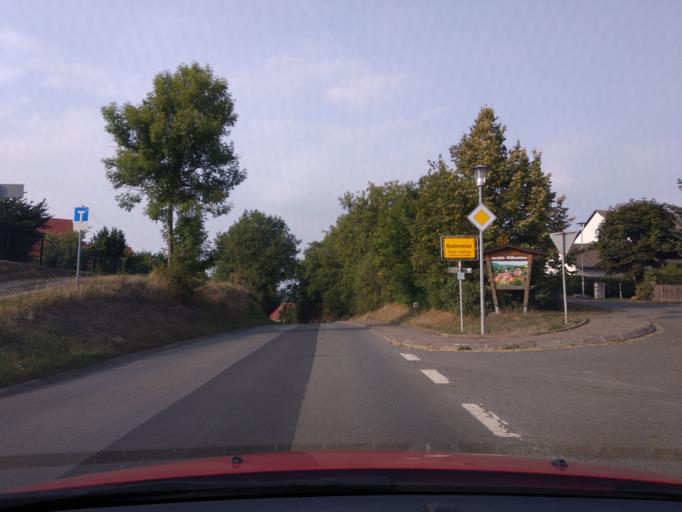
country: DE
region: Hesse
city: Liebenau
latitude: 51.4559
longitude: 9.3083
